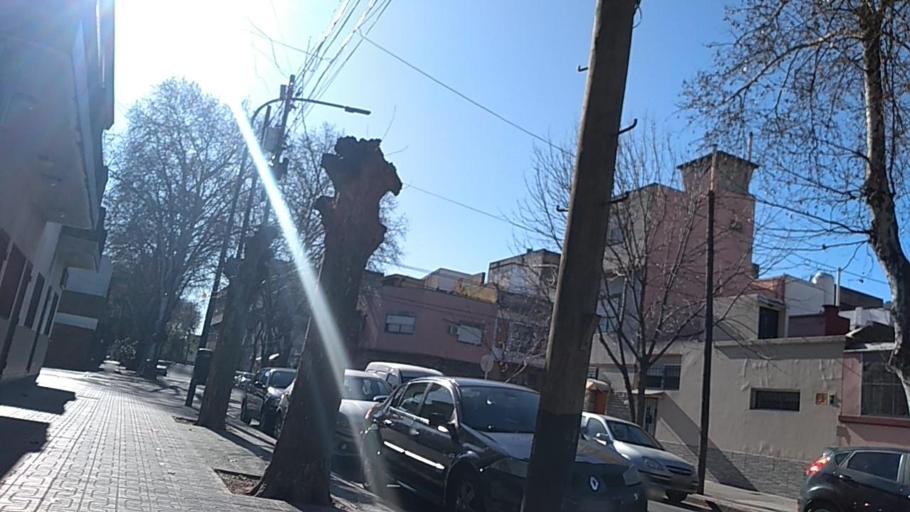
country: AR
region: Buenos Aires F.D.
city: Villa Santa Rita
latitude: -34.6203
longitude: -58.4908
